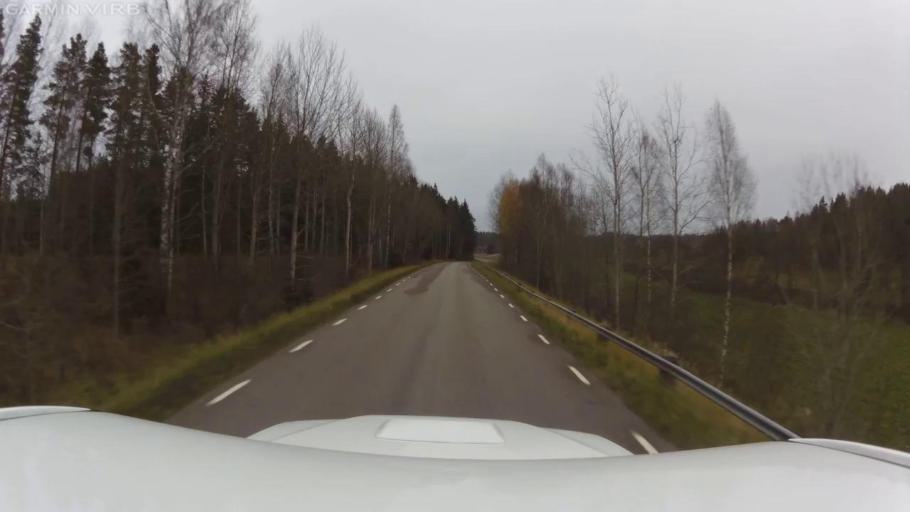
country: SE
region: OEstergoetland
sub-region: Linkopings Kommun
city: Vikingstad
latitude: 58.2229
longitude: 15.3967
